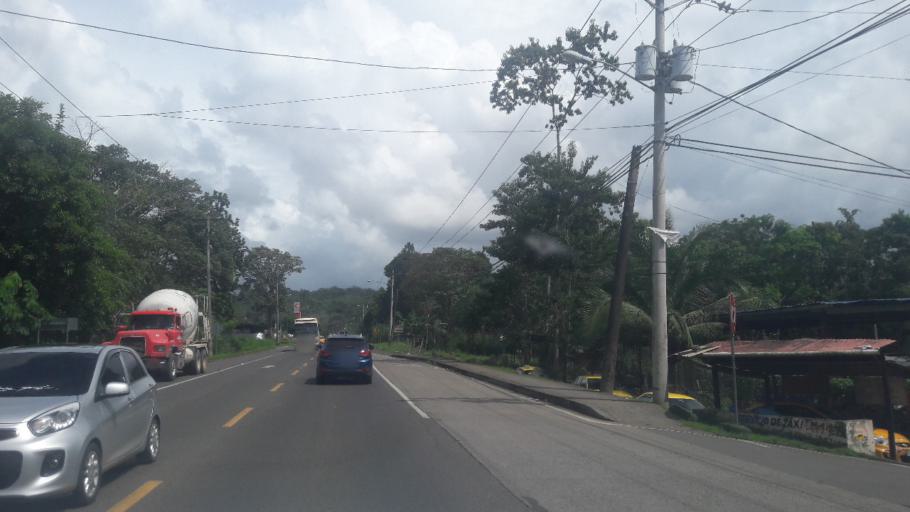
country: PA
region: Panama
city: Alcalde Diaz
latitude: 9.1251
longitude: -79.5877
